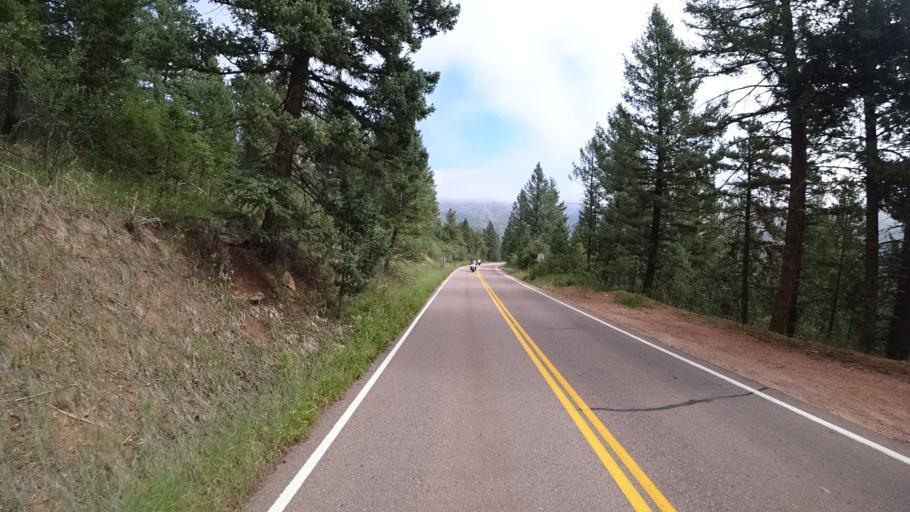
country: US
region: Colorado
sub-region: El Paso County
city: Cascade-Chipita Park
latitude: 38.9083
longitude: -104.9839
